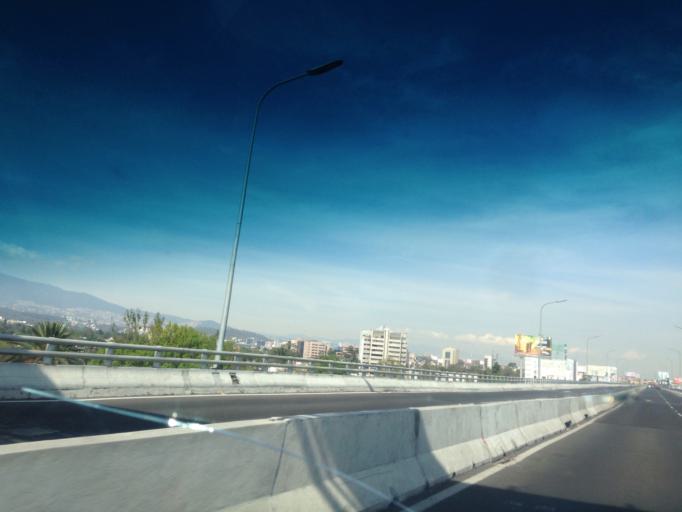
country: MX
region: Mexico City
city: Tlalpan
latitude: 19.2936
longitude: -99.1541
